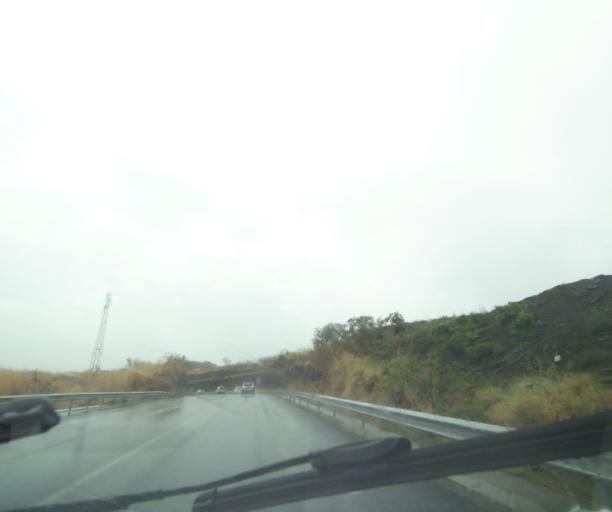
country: RE
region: Reunion
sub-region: Reunion
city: Le Port
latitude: -20.9713
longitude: 55.3132
